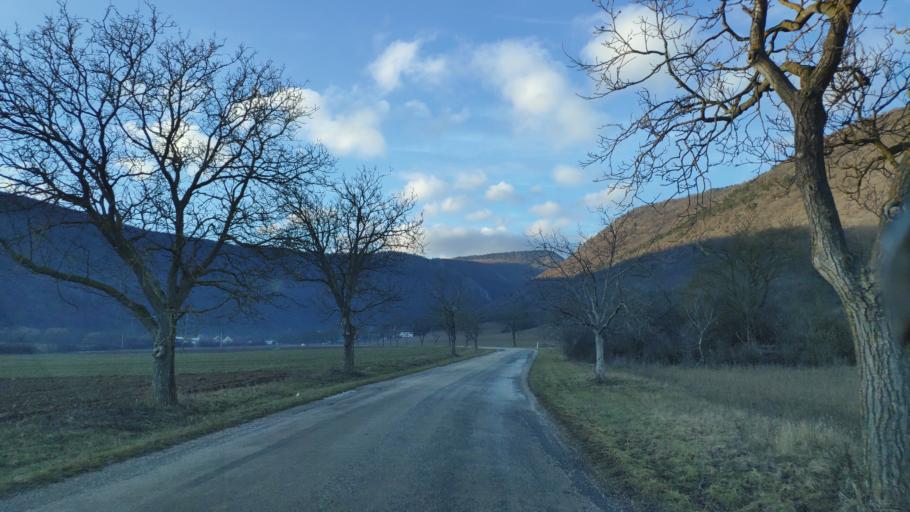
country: SK
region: Kosicky
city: Medzev
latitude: 48.6223
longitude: 20.8676
